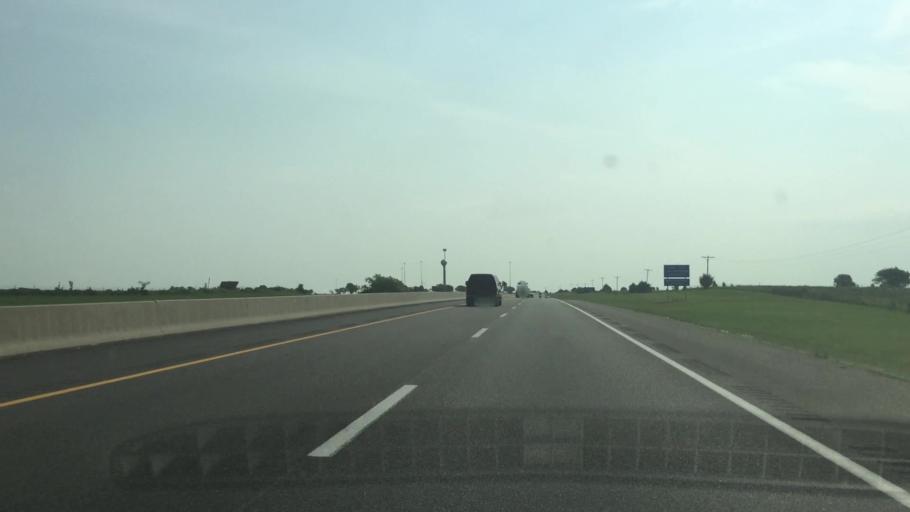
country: US
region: Kansas
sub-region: Butler County
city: Towanda
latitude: 37.7621
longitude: -96.9945
